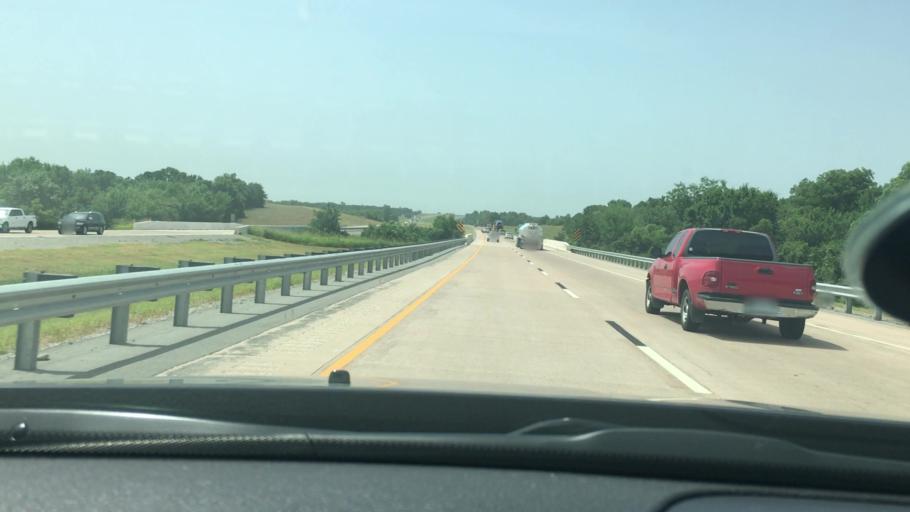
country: US
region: Oklahoma
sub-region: Garvin County
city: Wynnewood
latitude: 34.6467
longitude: -97.2202
